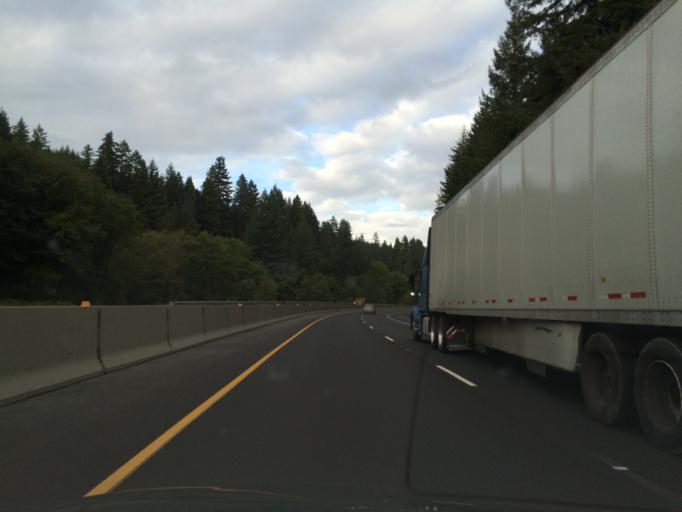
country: US
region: Oregon
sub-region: Lane County
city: Cottage Grove
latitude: 43.7518
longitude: -123.1641
